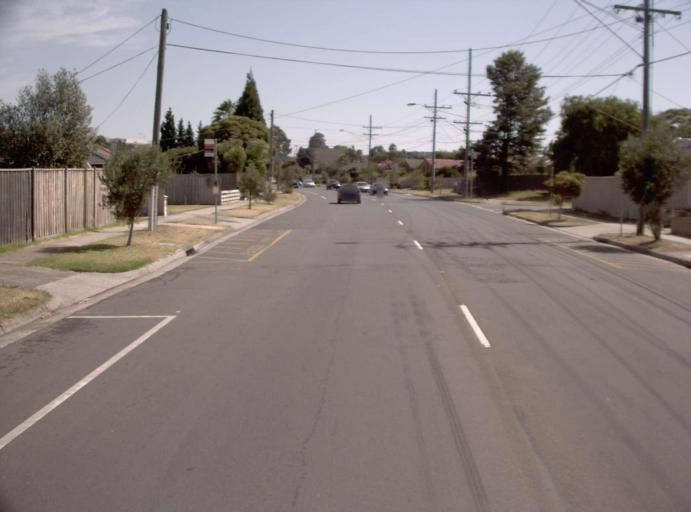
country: AU
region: Victoria
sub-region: Greater Dandenong
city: Noble Park North
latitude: -37.9416
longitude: 145.1925
